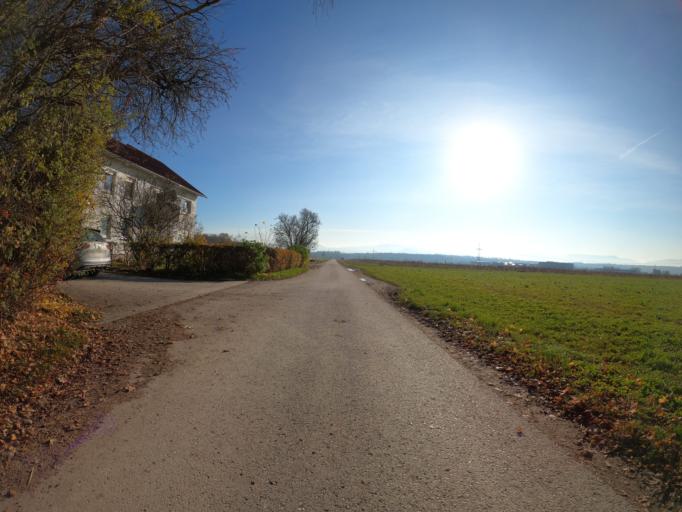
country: DE
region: Baden-Wuerttemberg
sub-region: Regierungsbezirk Stuttgart
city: Schlierbach
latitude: 48.6841
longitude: 9.5352
